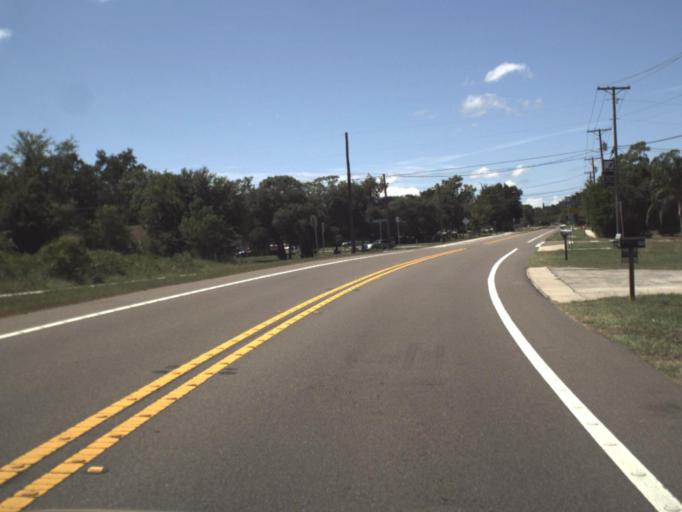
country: US
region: Florida
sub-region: Polk County
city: Babson Park
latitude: 27.8307
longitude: -81.5266
